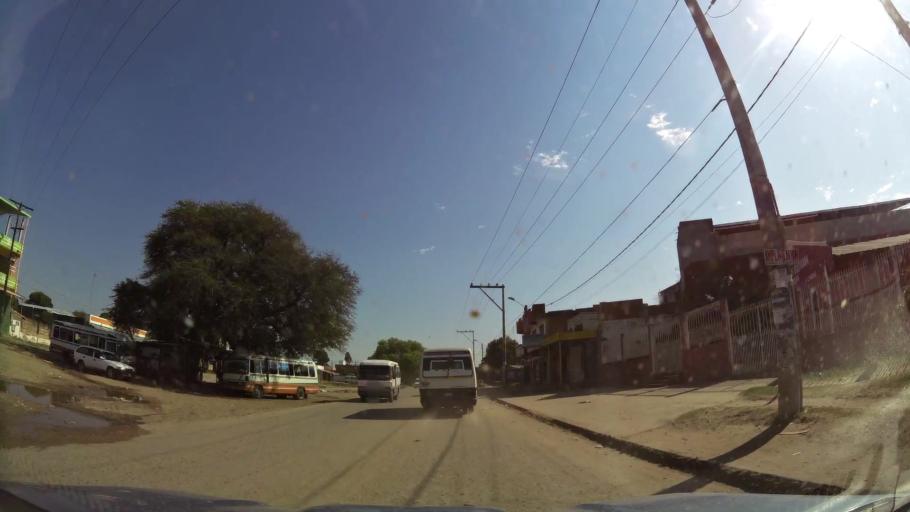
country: BO
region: Santa Cruz
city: Cotoca
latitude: -17.8185
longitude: -63.1192
